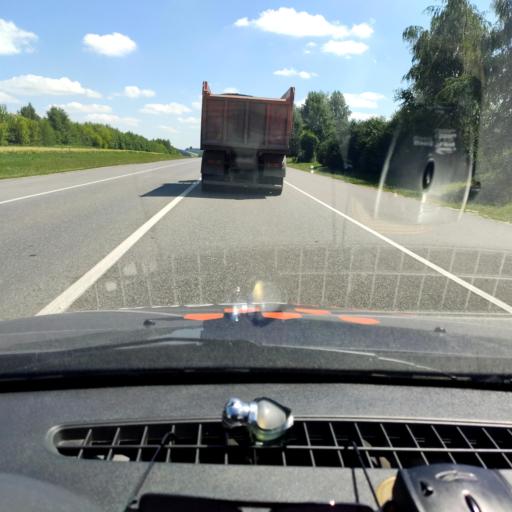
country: RU
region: Orjol
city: Zmiyevka
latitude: 52.8328
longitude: 36.2681
